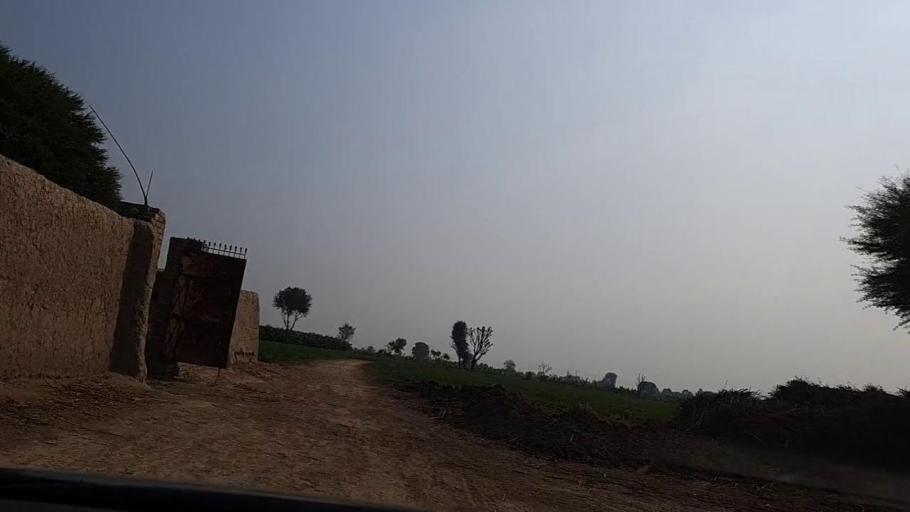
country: PK
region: Sindh
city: Sakrand
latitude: 26.1429
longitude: 68.2343
